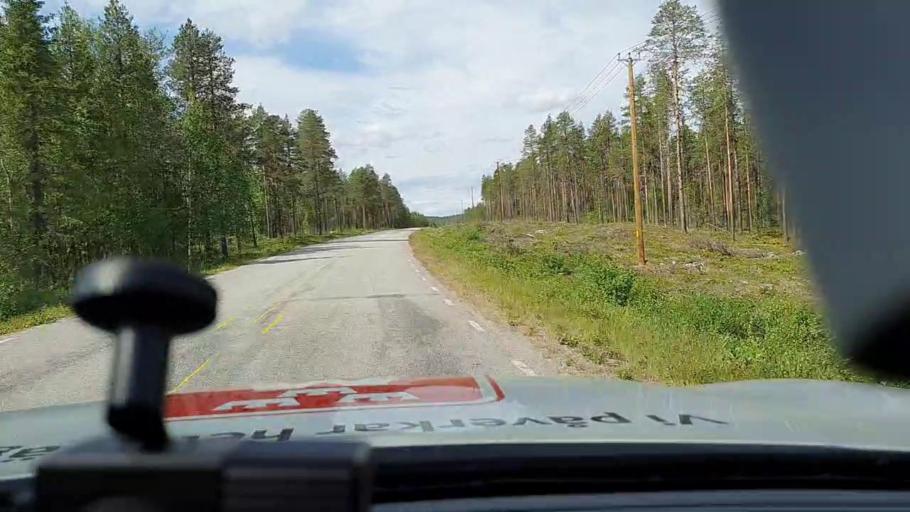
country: SE
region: Norrbotten
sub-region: Jokkmokks Kommun
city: Jokkmokk
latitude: 66.6233
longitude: 19.6858
